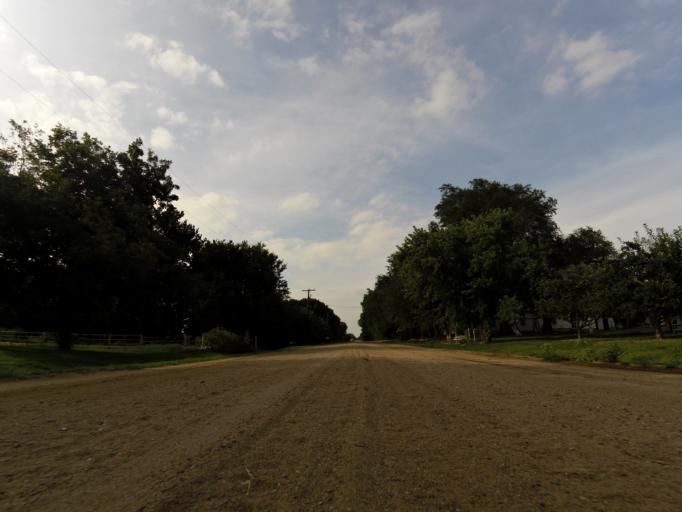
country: US
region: Kansas
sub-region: Reno County
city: South Hutchinson
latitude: 37.9887
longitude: -98.0686
